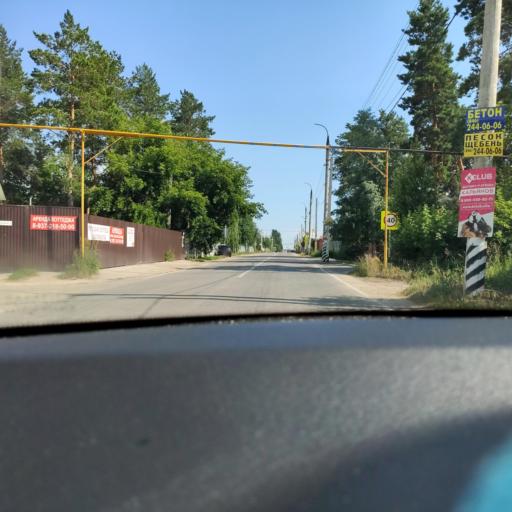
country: RU
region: Samara
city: Volzhskiy
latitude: 53.4520
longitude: 50.1723
